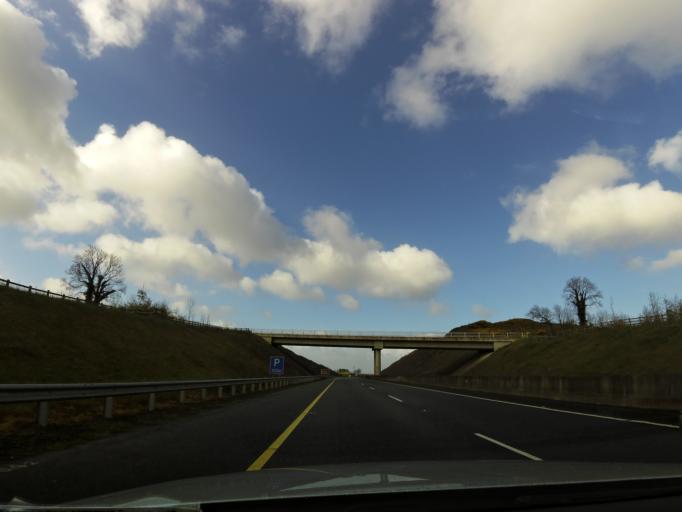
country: IE
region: Munster
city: Ballina
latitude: 52.7716
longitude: -8.3839
